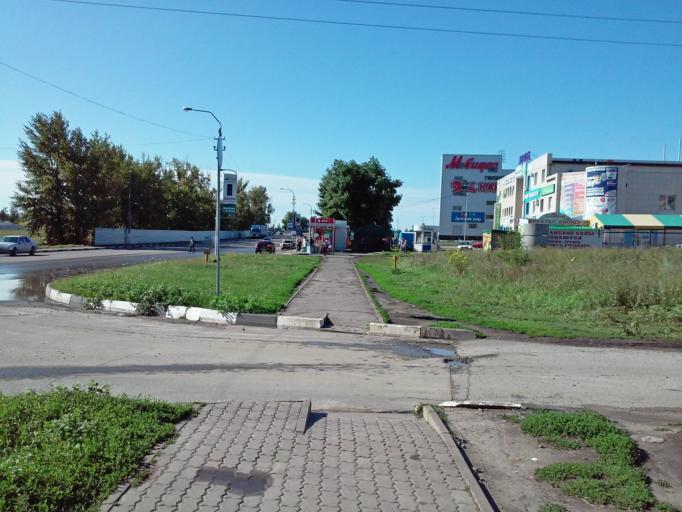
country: RU
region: Belgorod
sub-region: Belgorodskiy Rayon
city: Belgorod
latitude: 50.5543
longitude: 36.5725
